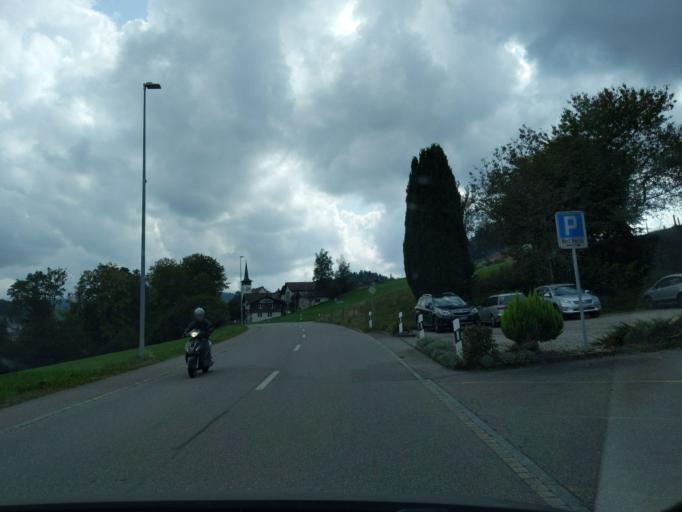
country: CH
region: Bern
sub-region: Oberaargau
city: Wyssachen
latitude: 47.0831
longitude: 7.8250
